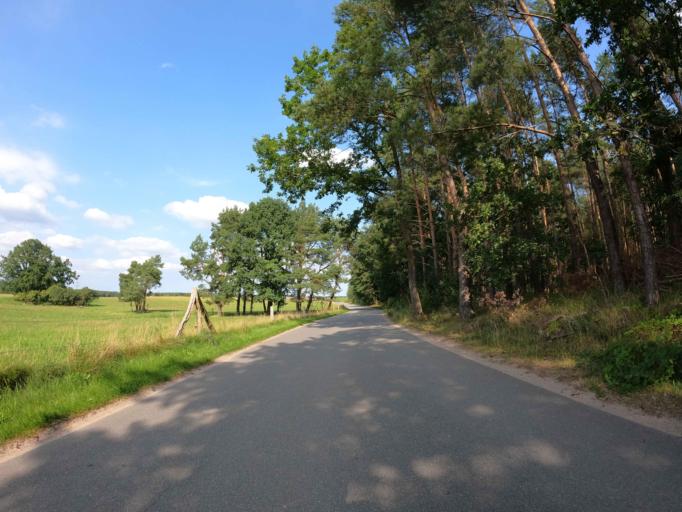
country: DE
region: Mecklenburg-Vorpommern
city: Malchow
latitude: 53.5123
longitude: 12.4415
